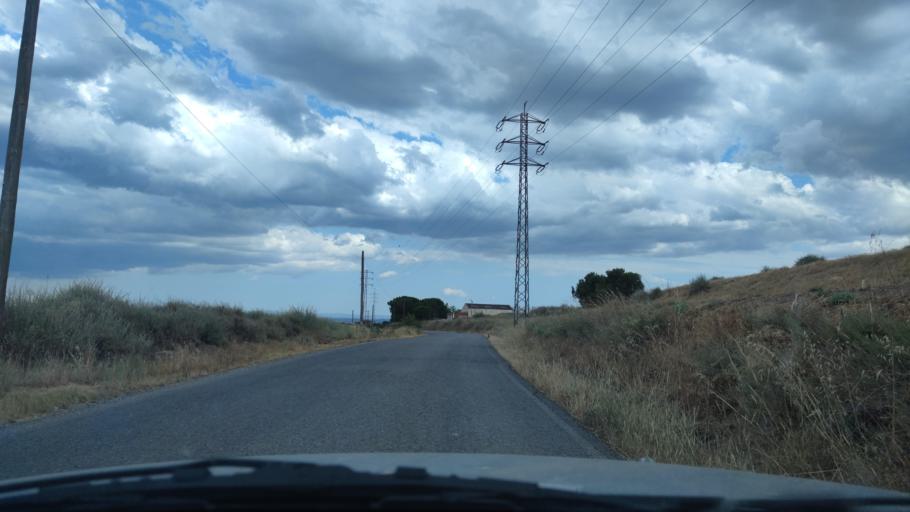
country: ES
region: Catalonia
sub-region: Provincia de Lleida
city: Lleida
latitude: 41.6148
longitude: 0.5780
